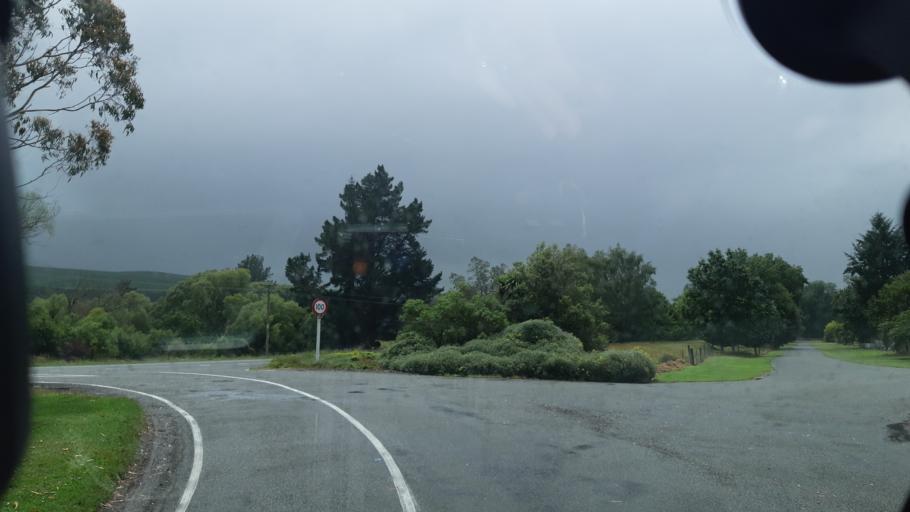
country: NZ
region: Canterbury
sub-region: Timaru District
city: Pleasant Point
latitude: -44.3097
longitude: 170.9536
